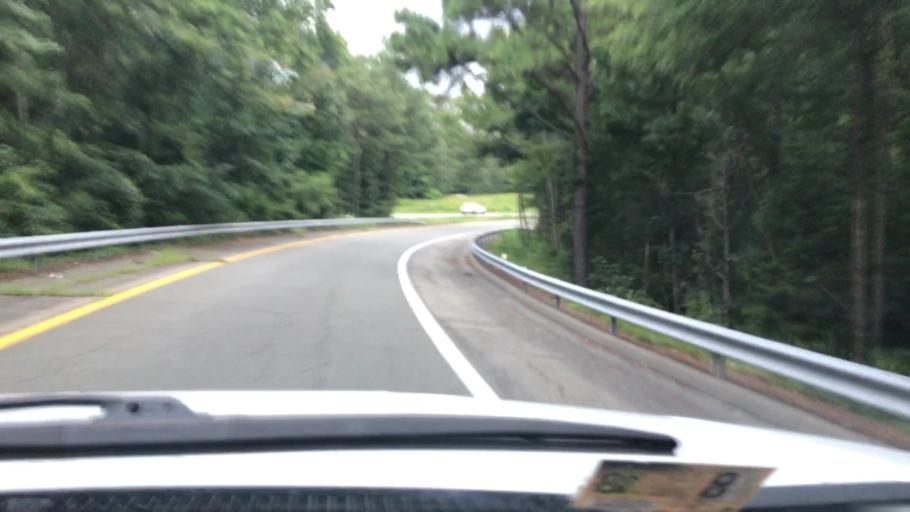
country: US
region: Virginia
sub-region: Henrico County
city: Short Pump
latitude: 37.6374
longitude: -77.5765
